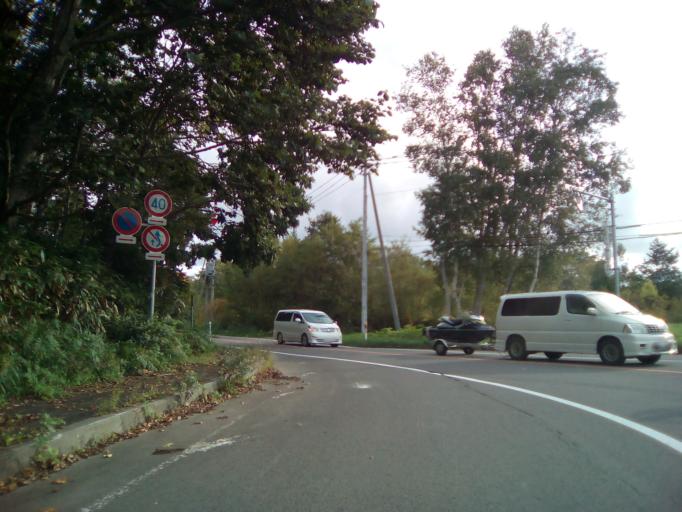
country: JP
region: Hokkaido
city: Date
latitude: 42.6672
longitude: 140.8382
